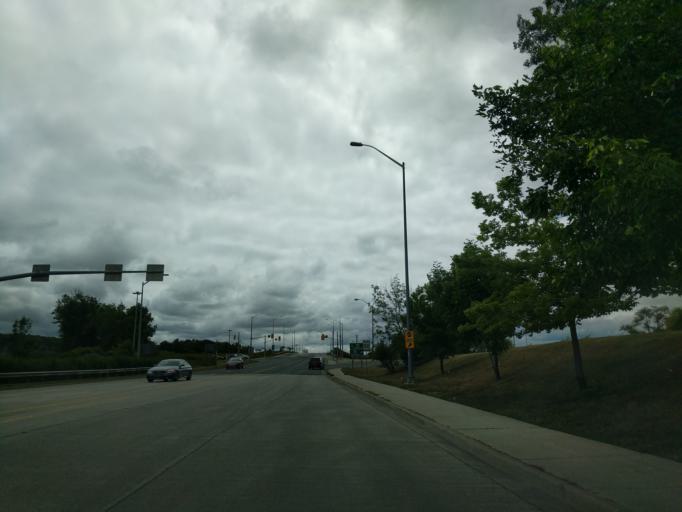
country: CA
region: Ontario
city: Thorold
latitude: 43.1599
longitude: -79.1628
